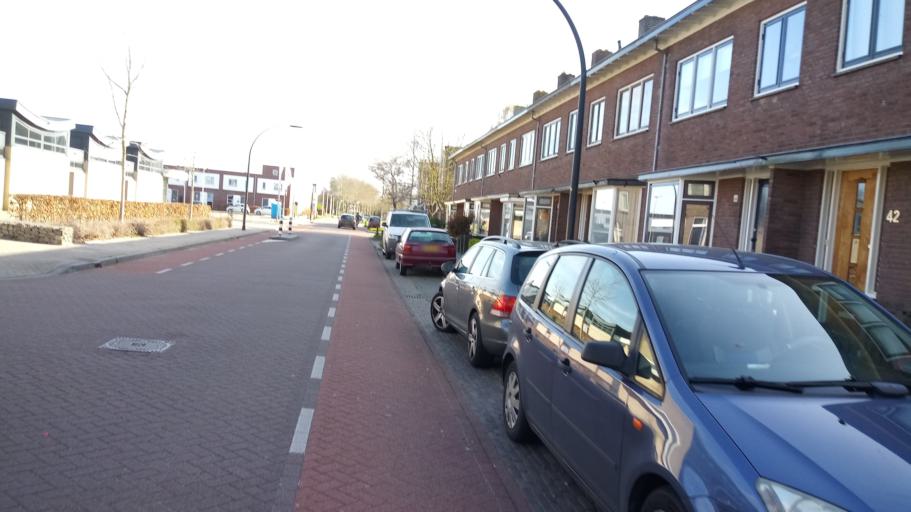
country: NL
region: Gelderland
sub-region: Gemeente Zutphen
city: Zutphen
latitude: 52.1402
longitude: 6.2098
